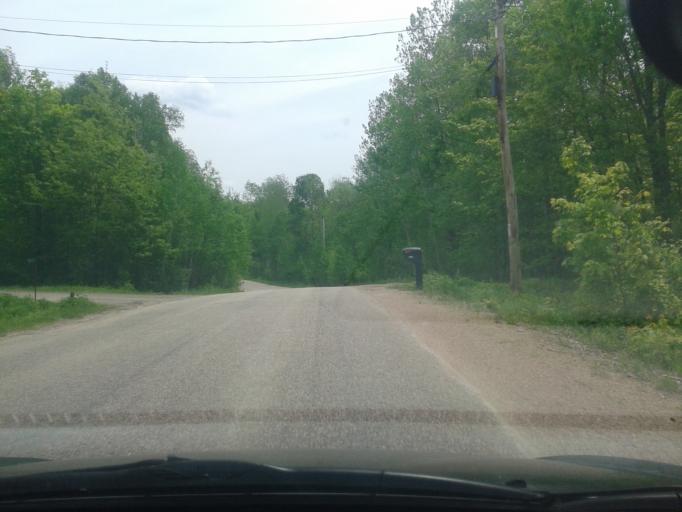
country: CA
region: Ontario
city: Powassan
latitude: 46.1856
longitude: -79.2257
